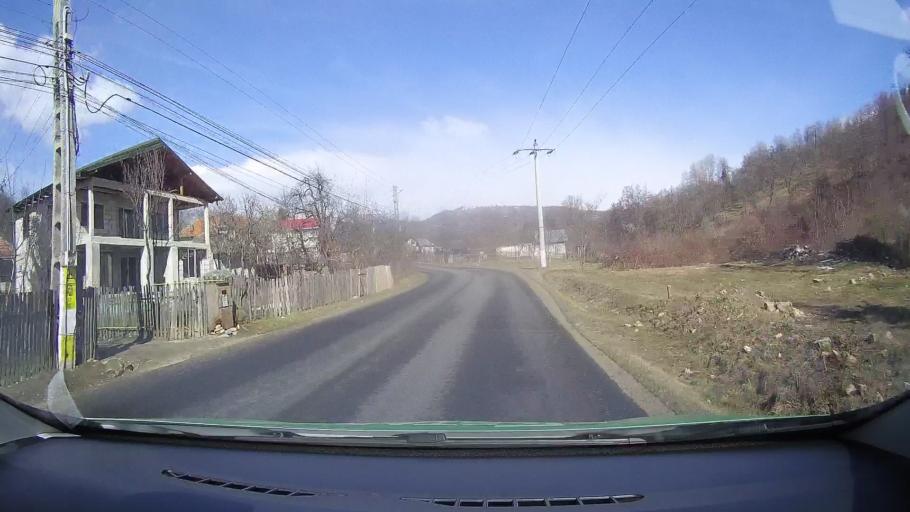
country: RO
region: Dambovita
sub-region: Comuna Runcu
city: Badeni
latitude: 45.1665
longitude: 25.3952
